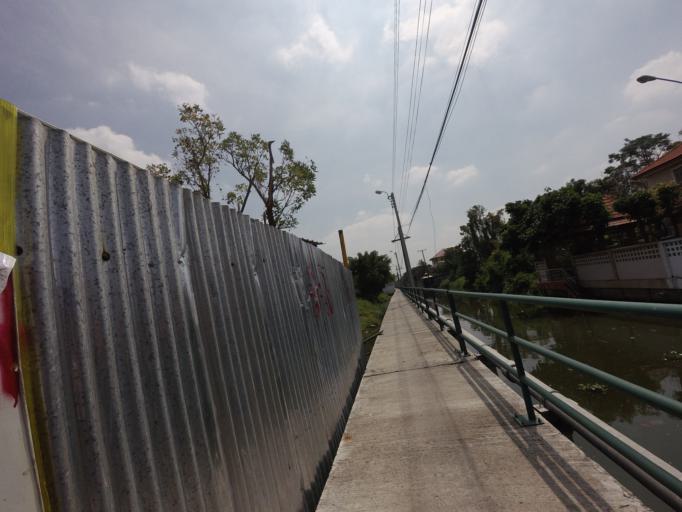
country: TH
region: Bangkok
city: Bueng Kum
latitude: 13.7704
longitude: 100.6671
